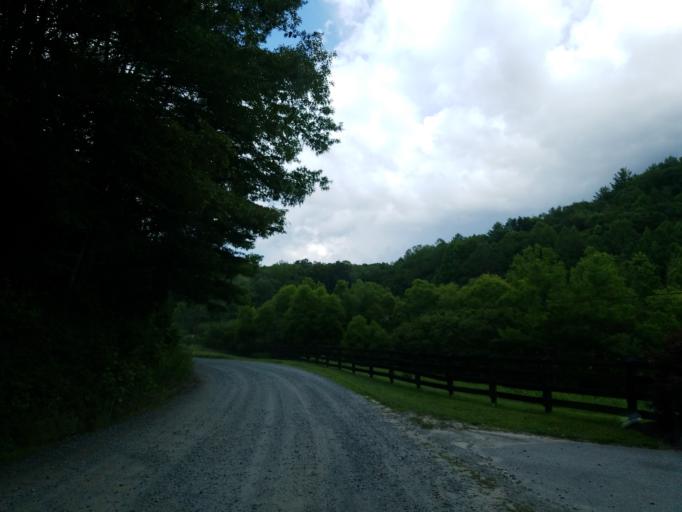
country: US
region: Georgia
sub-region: Fannin County
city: Blue Ridge
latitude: 34.7805
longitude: -84.3591
